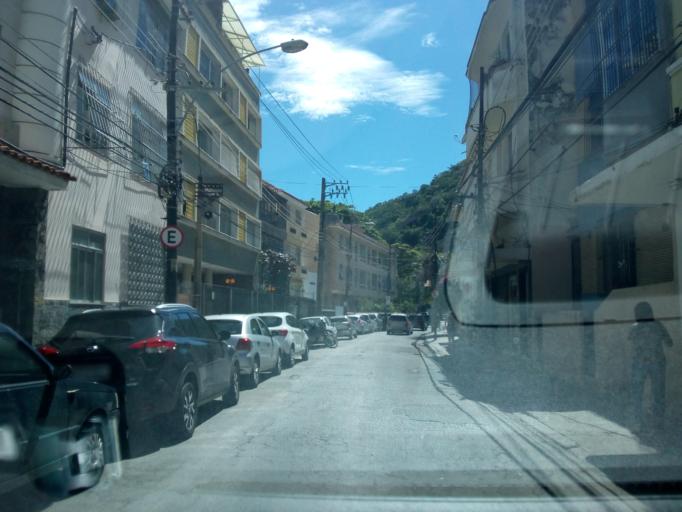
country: BR
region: Rio de Janeiro
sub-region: Rio De Janeiro
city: Rio de Janeiro
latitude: -22.9485
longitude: -43.1653
